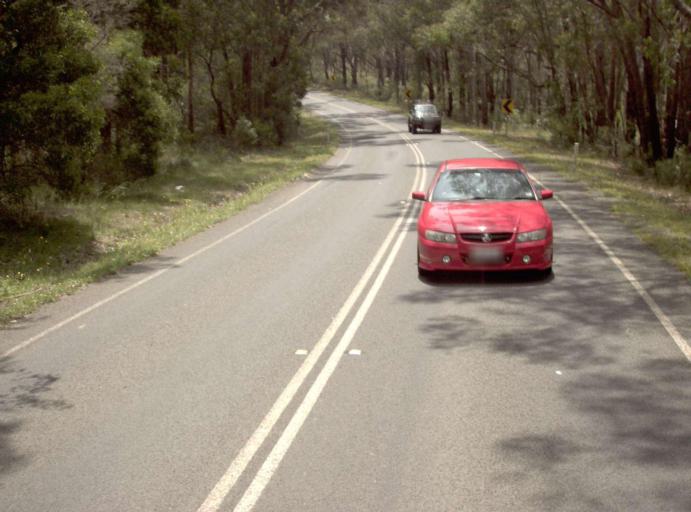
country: AU
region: Victoria
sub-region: Latrobe
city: Traralgon
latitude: -38.4090
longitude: 146.7519
